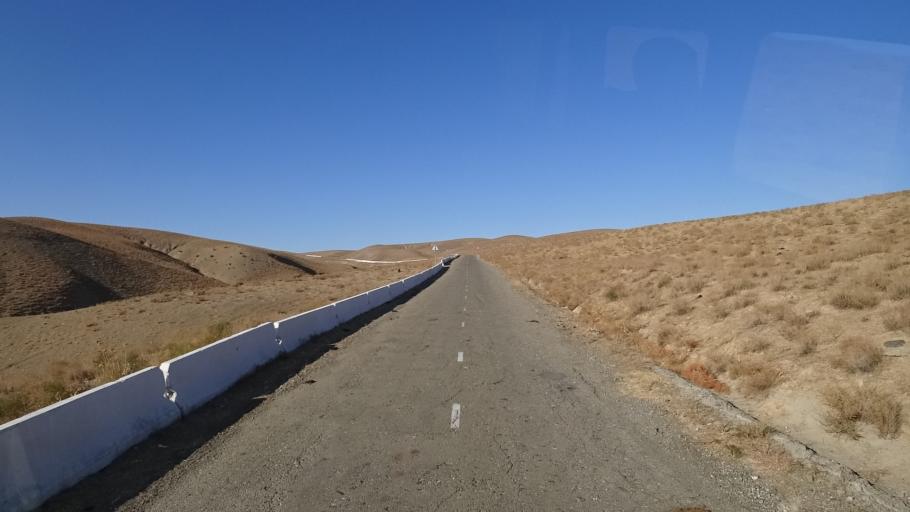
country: UZ
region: Navoiy
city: Karmana Shahri
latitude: 40.2742
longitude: 65.5770
